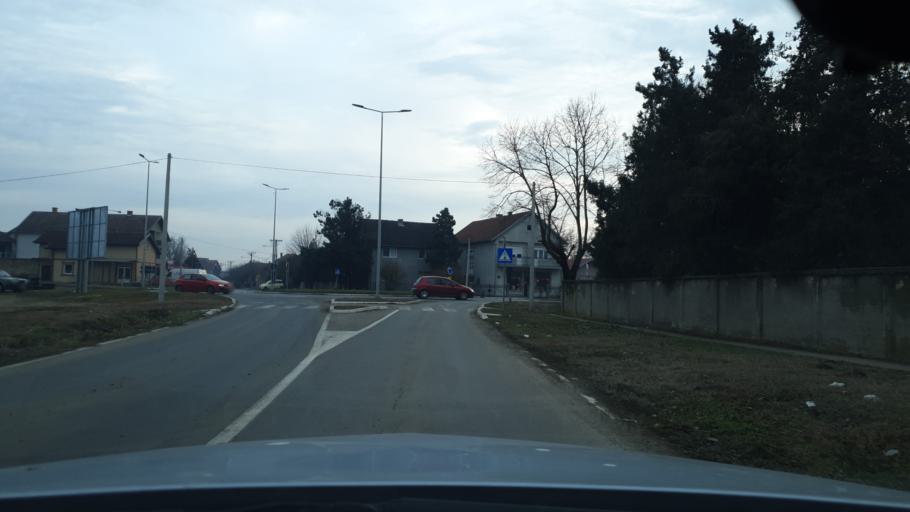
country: RS
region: Autonomna Pokrajina Vojvodina
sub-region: Sremski Okrug
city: Stara Pazova
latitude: 44.9876
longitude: 20.1828
